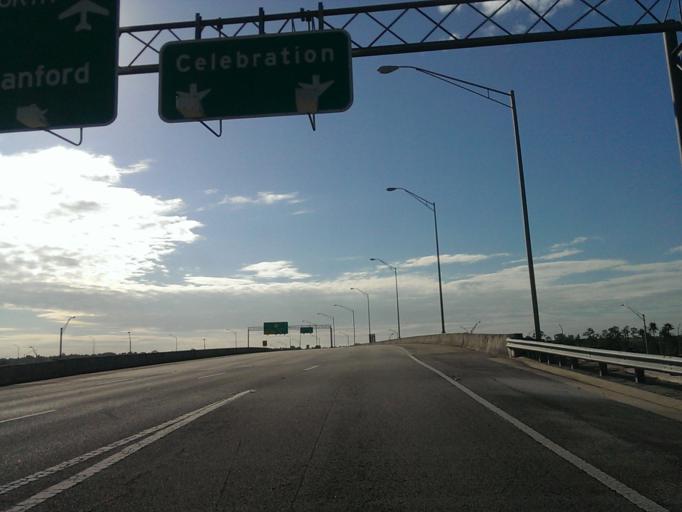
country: US
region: Florida
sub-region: Osceola County
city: Celebration
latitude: 28.3066
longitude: -81.5716
